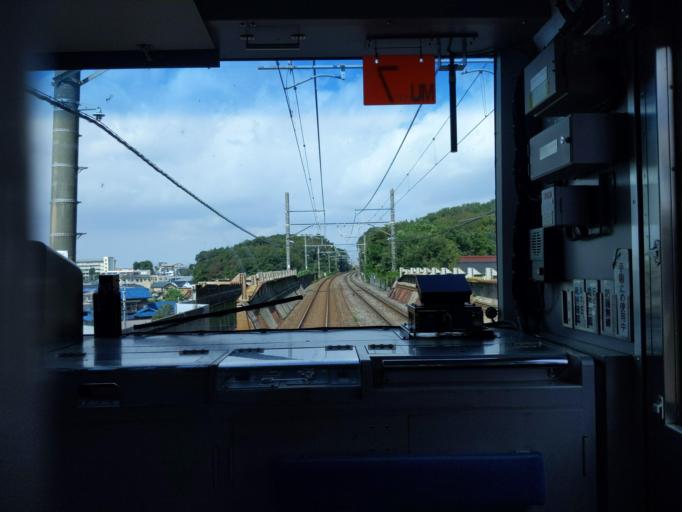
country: JP
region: Chiba
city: Matsudo
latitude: 35.7722
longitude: 139.9433
